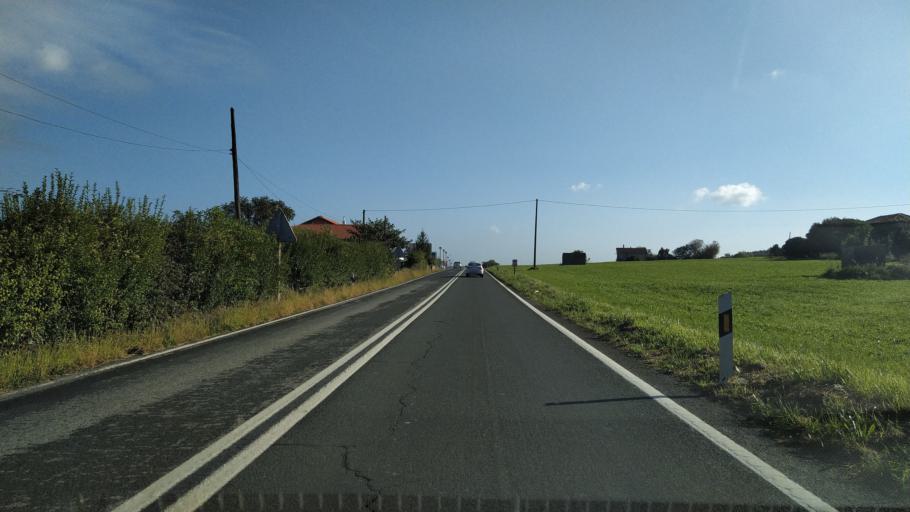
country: ES
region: Cantabria
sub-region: Provincia de Cantabria
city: Santa Cruz de Bezana
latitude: 43.4320
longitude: -3.9152
